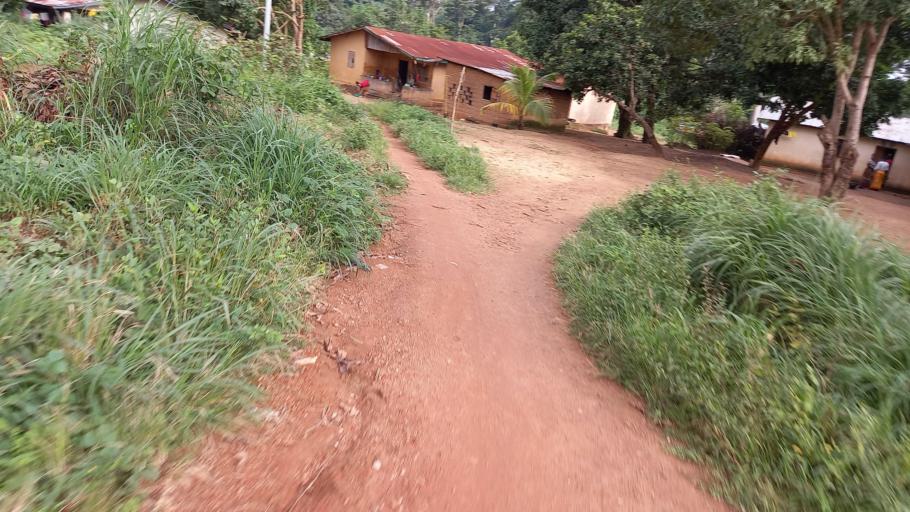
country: SL
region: Eastern Province
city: Kailahun
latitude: 8.2787
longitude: -10.5794
